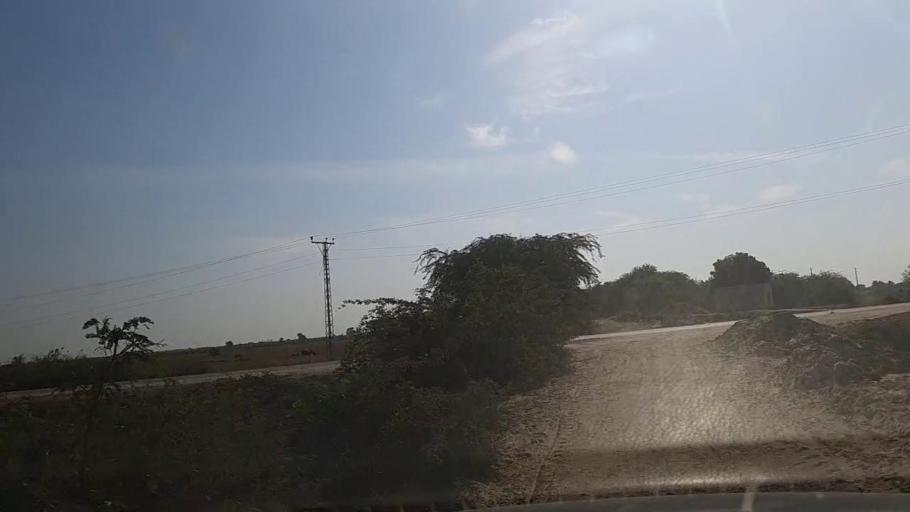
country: PK
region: Sindh
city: Bulri
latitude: 24.8363
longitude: 68.2809
